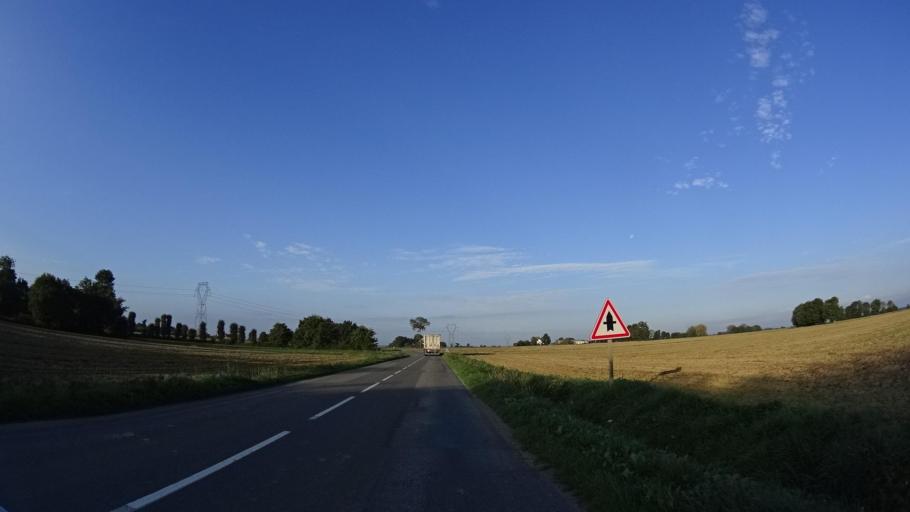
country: FR
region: Brittany
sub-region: Departement d'Ille-et-Vilaine
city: Quedillac
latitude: 48.2577
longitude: -2.1113
